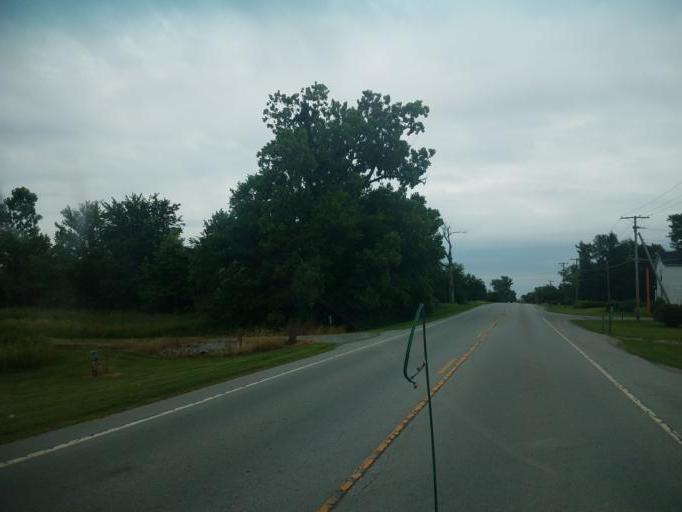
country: US
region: Ohio
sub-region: Hardin County
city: Ada
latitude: 40.7539
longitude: -83.8232
